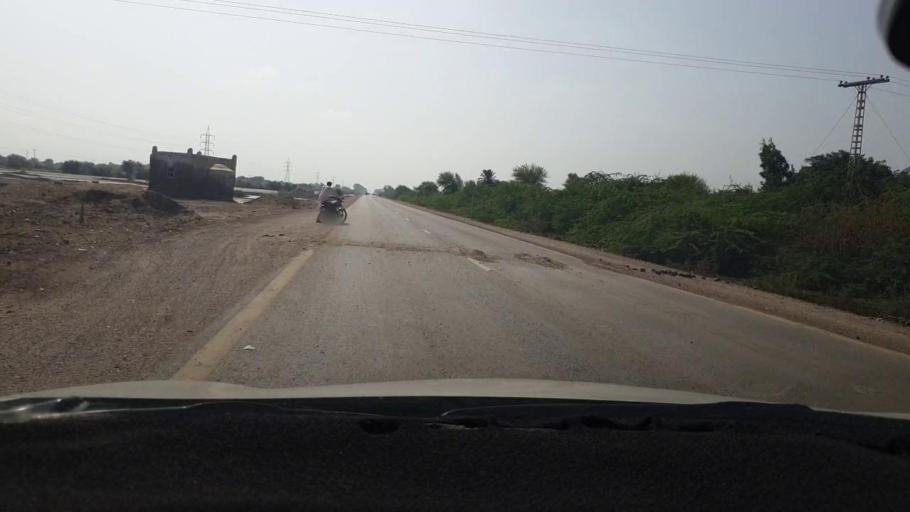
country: PK
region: Sindh
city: Jhol
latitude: 25.9113
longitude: 69.0129
